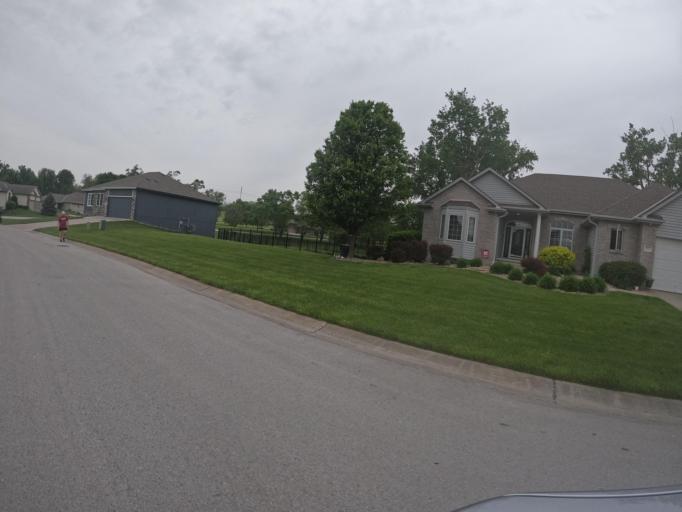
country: US
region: Nebraska
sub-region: Sarpy County
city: Offutt Air Force Base
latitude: 41.0481
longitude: -95.9549
